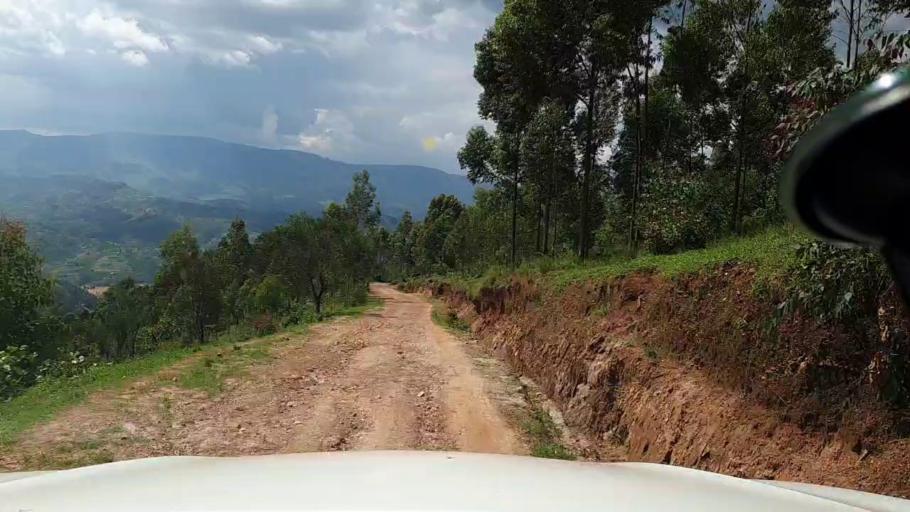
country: RW
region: Southern Province
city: Gitarama
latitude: -1.8414
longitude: 29.8222
